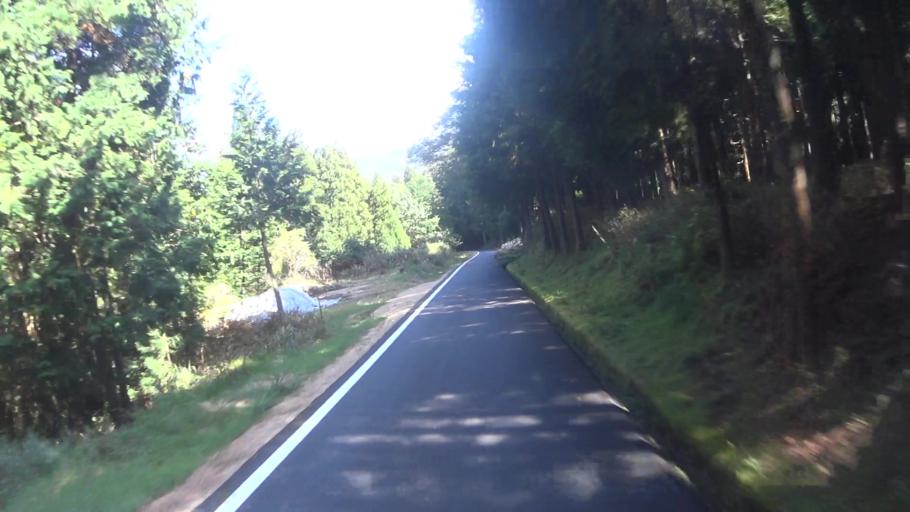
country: JP
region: Hyogo
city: Toyooka
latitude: 35.5436
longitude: 134.9698
